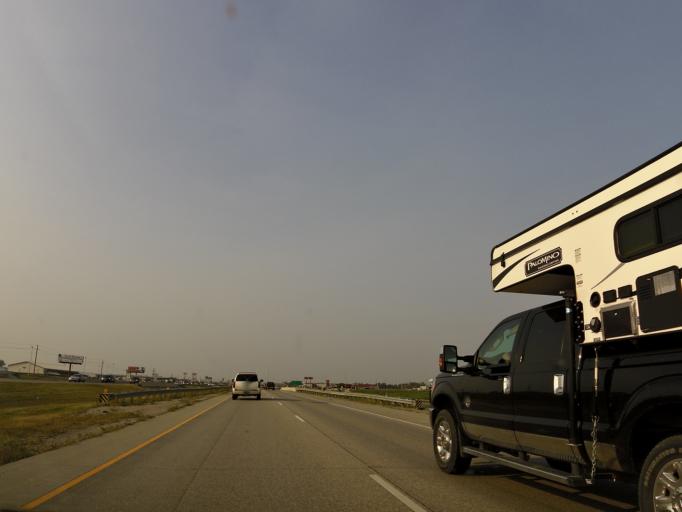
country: US
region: North Dakota
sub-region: Cass County
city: Fargo
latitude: 46.8170
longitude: -96.8393
